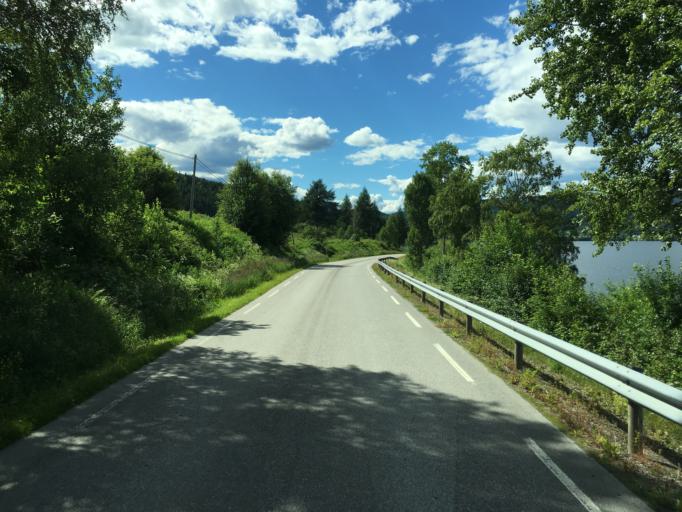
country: NO
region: Oppland
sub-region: Sondre Land
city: Hov
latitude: 60.5114
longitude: 10.3300
